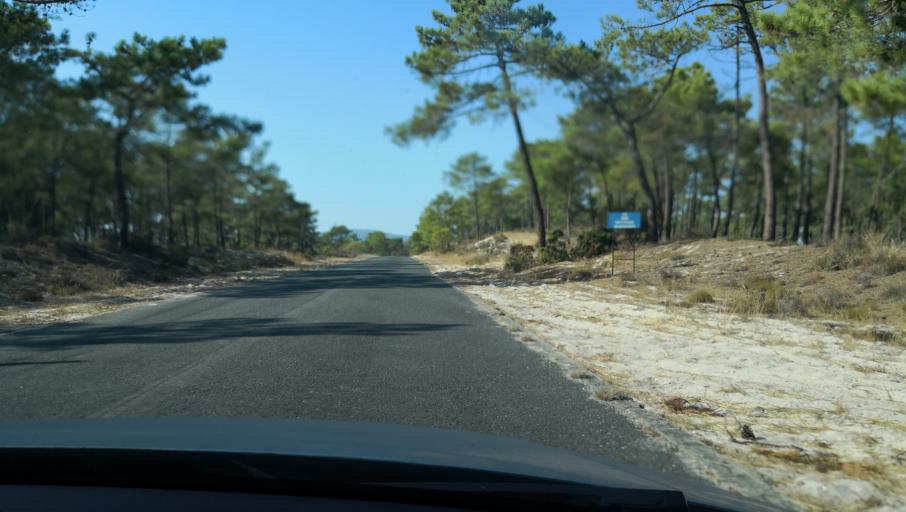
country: PT
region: Setubal
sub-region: Setubal
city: Setubal
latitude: 38.4706
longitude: -8.8719
